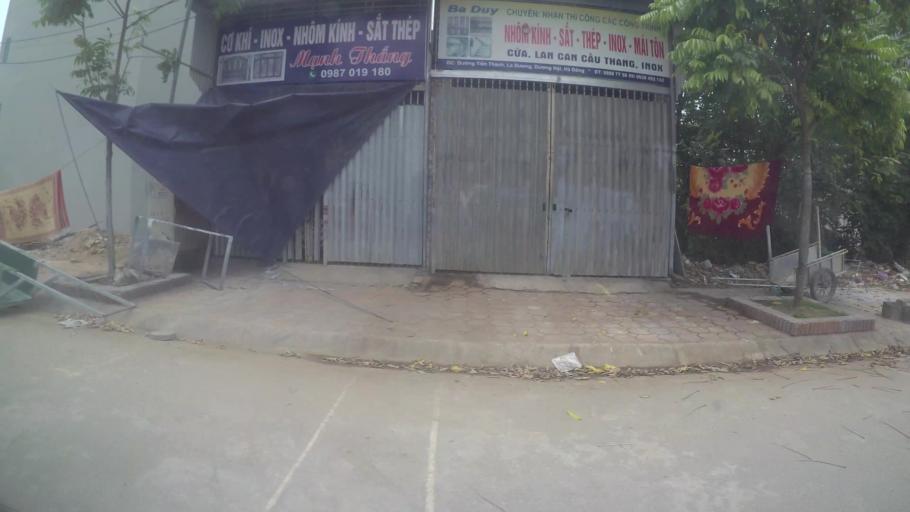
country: VN
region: Ha Noi
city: Ha Dong
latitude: 20.9898
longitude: 105.7426
